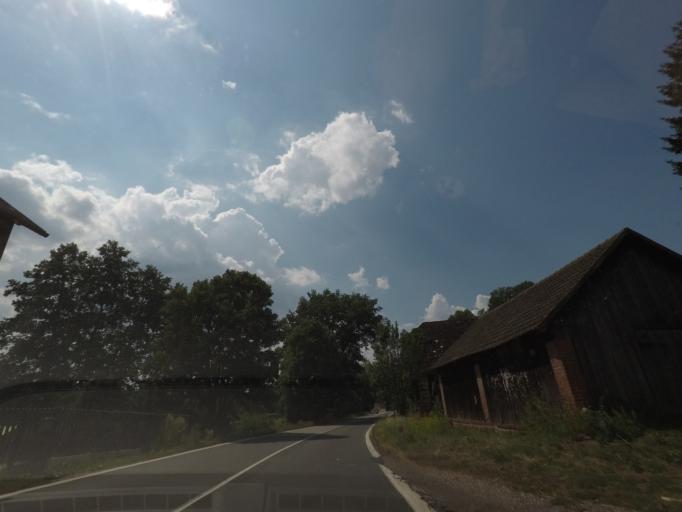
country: CZ
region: Kralovehradecky
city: Pilnikov
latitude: 50.5420
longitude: 15.8335
